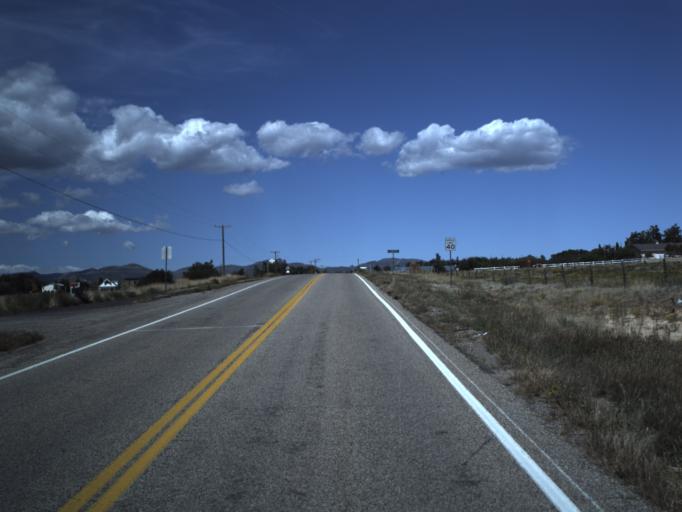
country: US
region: Utah
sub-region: Washington County
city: Ivins
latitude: 37.3337
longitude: -113.6932
